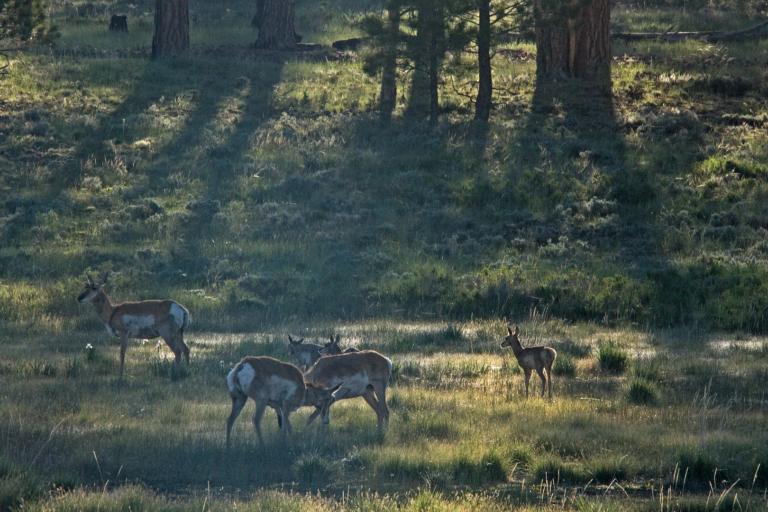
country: US
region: Utah
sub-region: Garfield County
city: Panguitch
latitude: 37.6360
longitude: -112.1723
